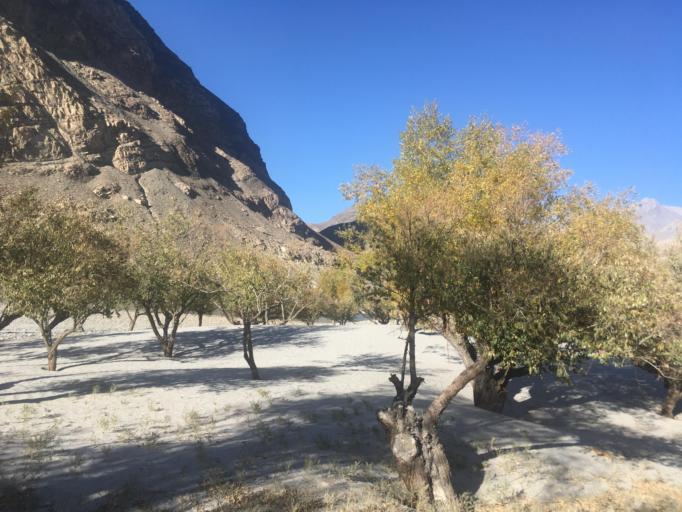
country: PK
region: Gilgit-Baltistan
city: Skardu
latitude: 35.3178
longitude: 75.6883
